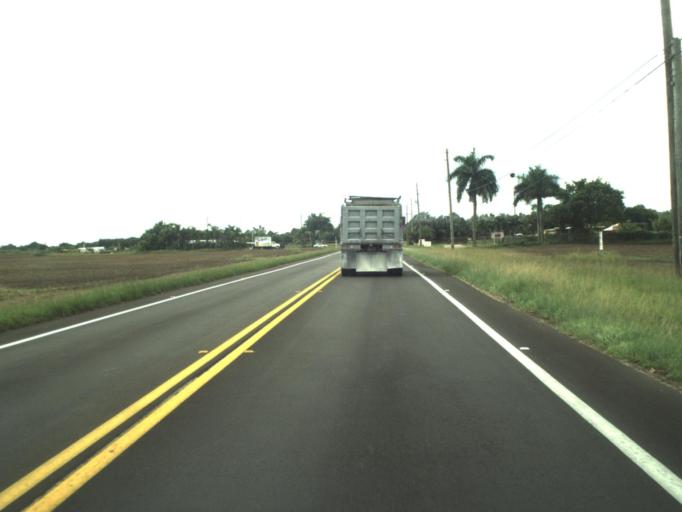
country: US
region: Florida
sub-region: Miami-Dade County
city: Richmond West
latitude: 25.6009
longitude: -80.4788
